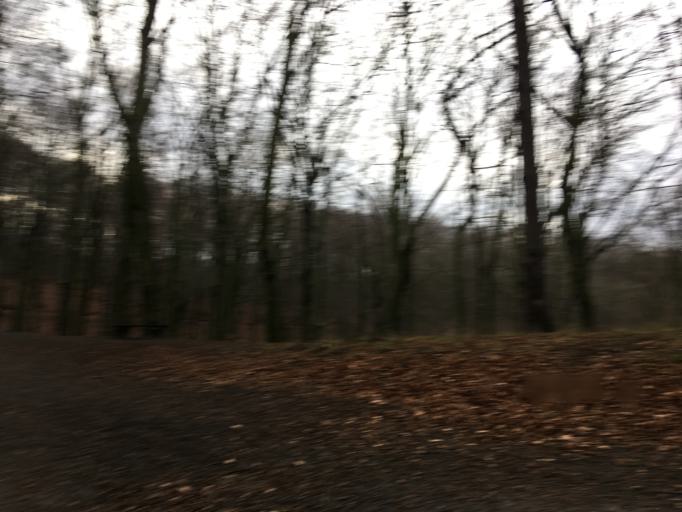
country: PL
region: Pomeranian Voivodeship
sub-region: Gdansk
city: Gdansk
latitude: 54.3724
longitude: 18.6061
